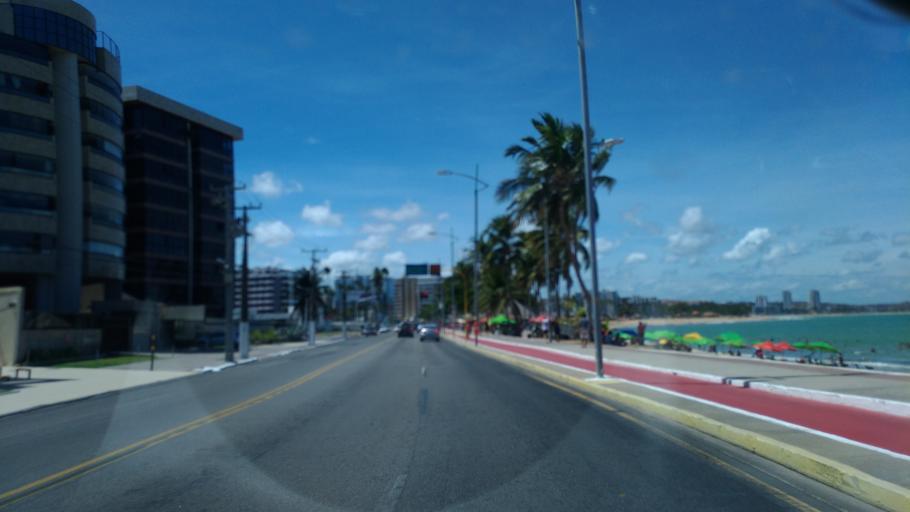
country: BR
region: Alagoas
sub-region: Maceio
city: Maceio
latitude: -9.6522
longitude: -35.6990
